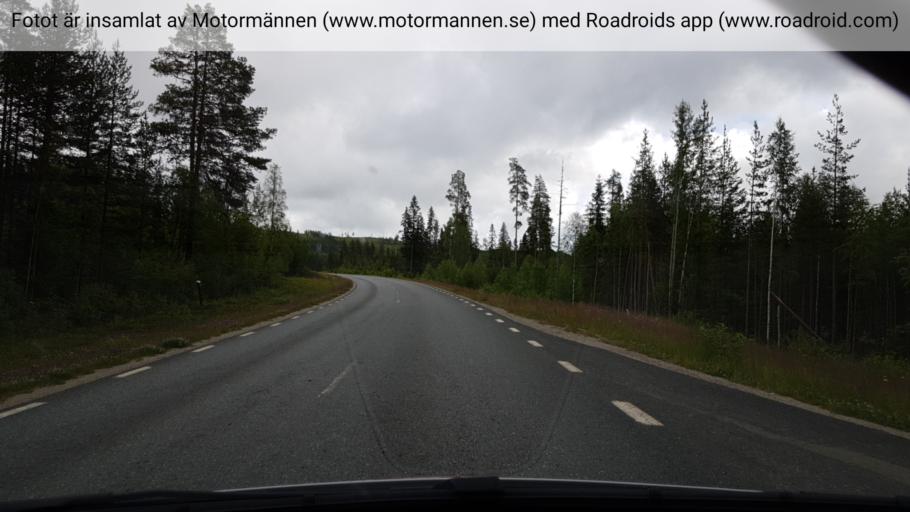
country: SE
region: Vaesterbotten
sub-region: Lycksele Kommun
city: Lycksele
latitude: 64.4293
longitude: 18.9803
